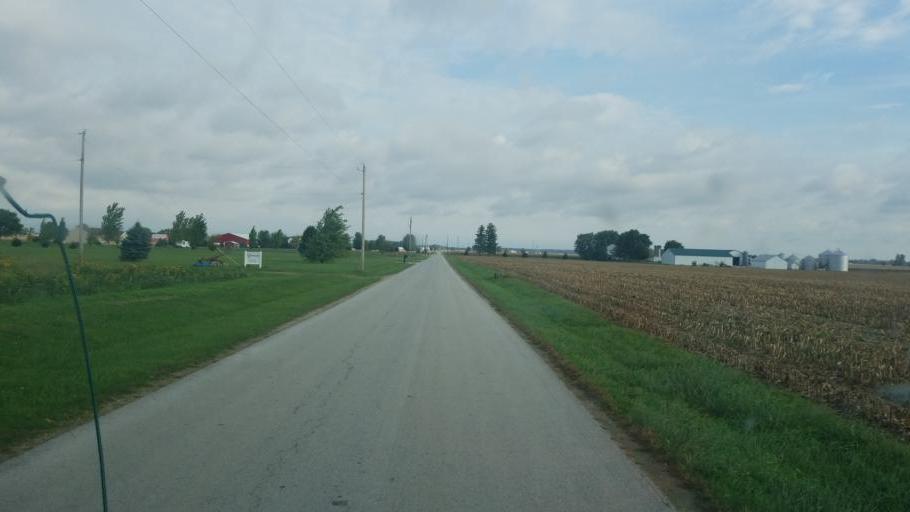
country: US
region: Ohio
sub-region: Wyandot County
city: Carey
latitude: 40.9814
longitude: -83.4296
